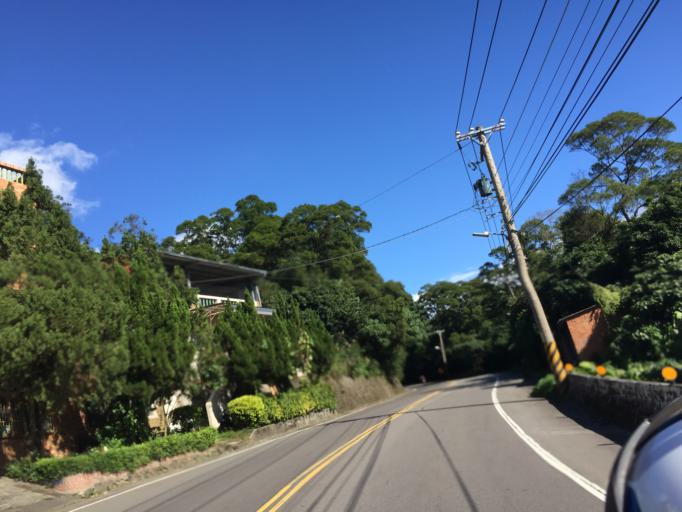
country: TW
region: Taipei
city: Taipei
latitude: 25.1824
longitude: 121.4667
